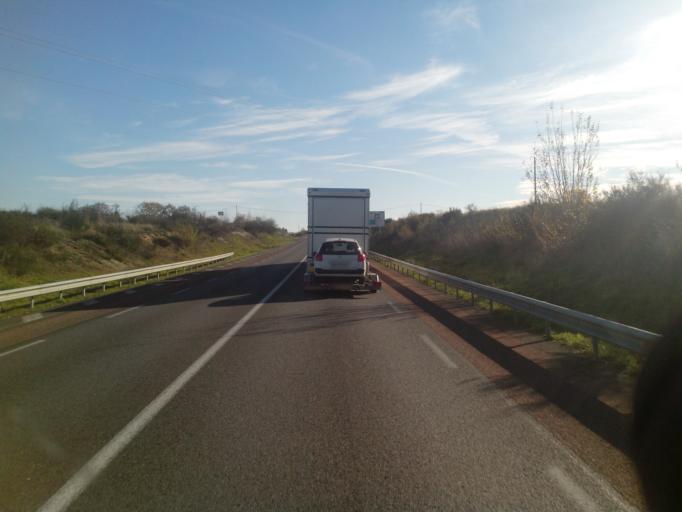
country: FR
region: Limousin
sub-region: Departement de la Haute-Vienne
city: Bellac
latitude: 46.1279
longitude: 1.0718
